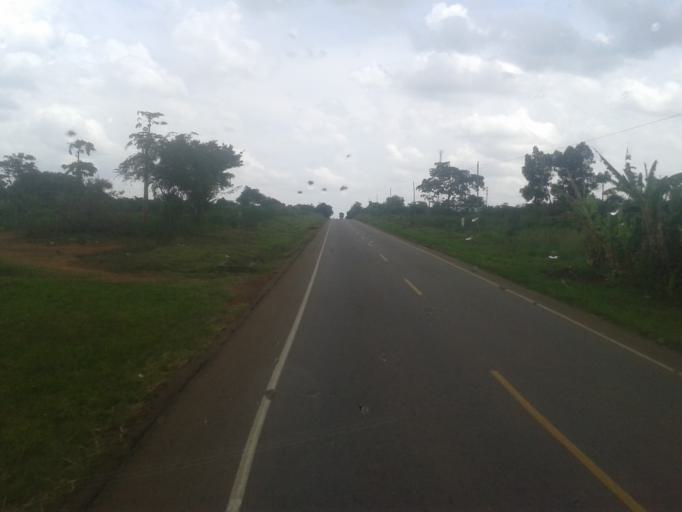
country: UG
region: Central Region
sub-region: Nakasongola District
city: Nakasongola
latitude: 1.3529
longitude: 32.3793
